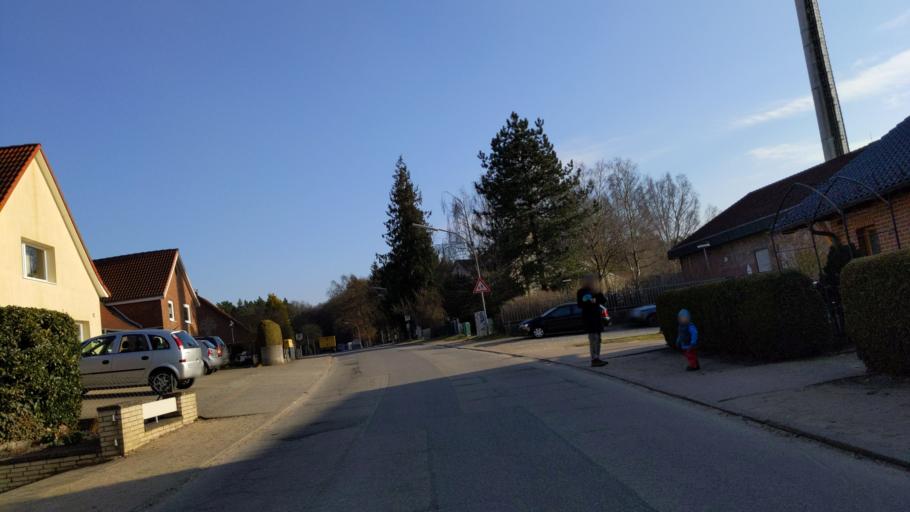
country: DE
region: Schleswig-Holstein
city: Ratekau
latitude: 53.9719
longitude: 10.7022
